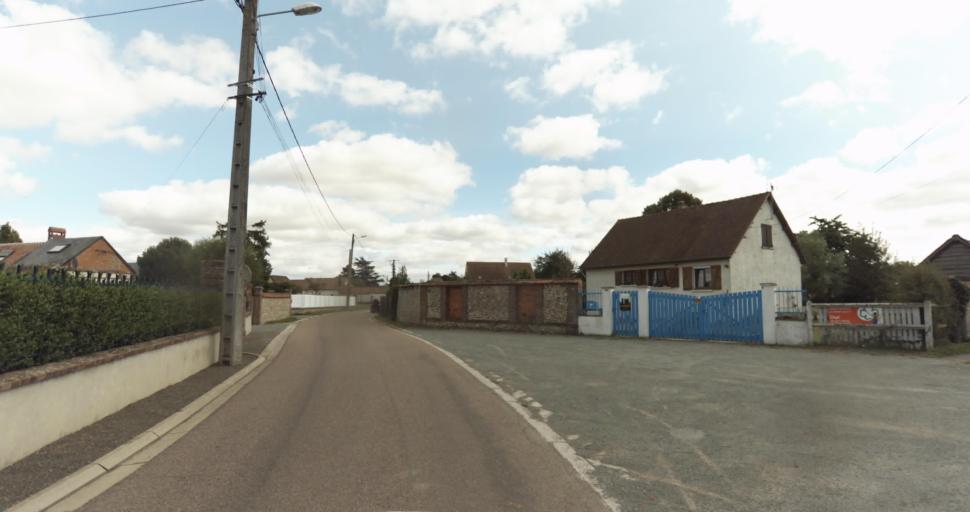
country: FR
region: Haute-Normandie
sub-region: Departement de l'Eure
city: La Madeleine-de-Nonancourt
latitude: 48.8294
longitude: 1.1762
